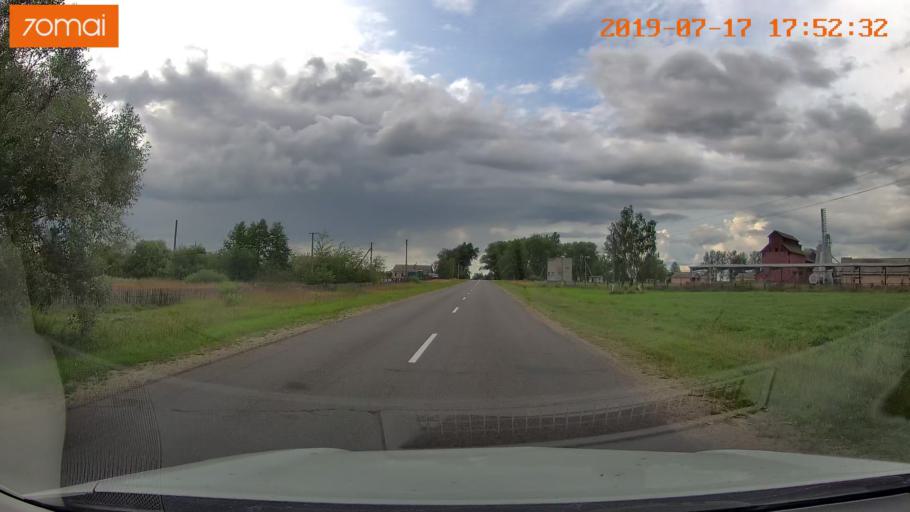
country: BY
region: Mogilev
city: Hlusha
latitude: 53.1660
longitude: 28.7814
